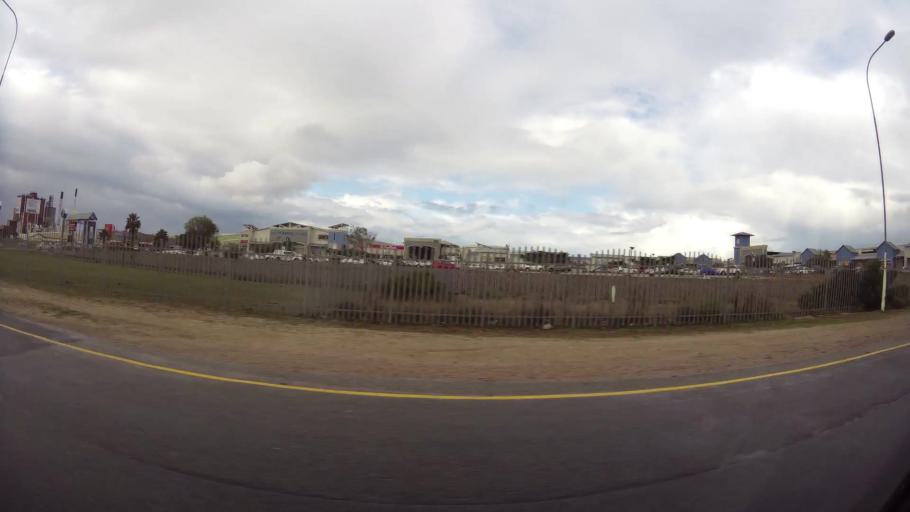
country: ZA
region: Western Cape
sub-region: Eden District Municipality
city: Mossel Bay
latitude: -34.1478
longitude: 22.1021
